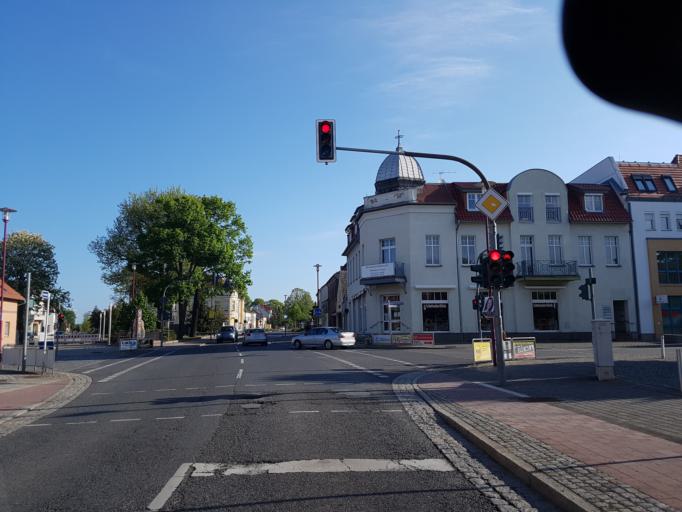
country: DE
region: Brandenburg
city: Grossraschen
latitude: 51.5876
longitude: 14.0110
